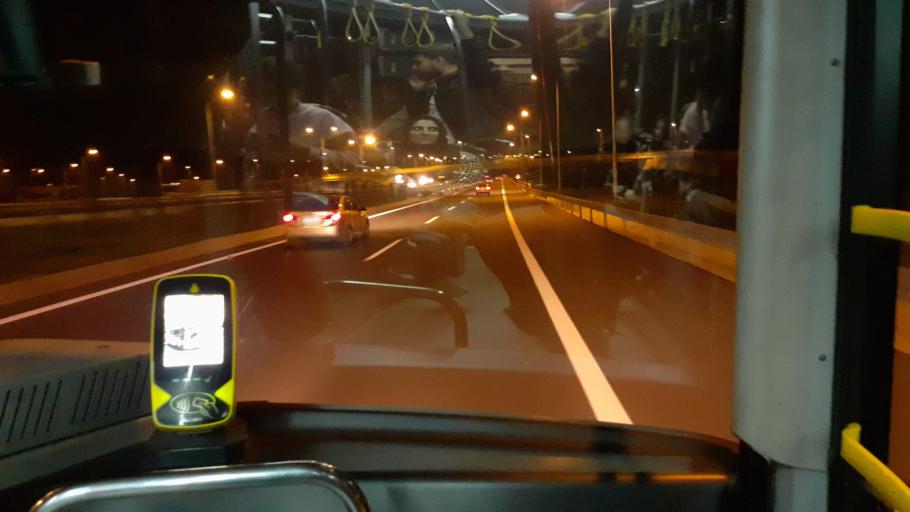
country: TR
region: Istanbul
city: Durusu
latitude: 41.2421
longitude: 28.7636
